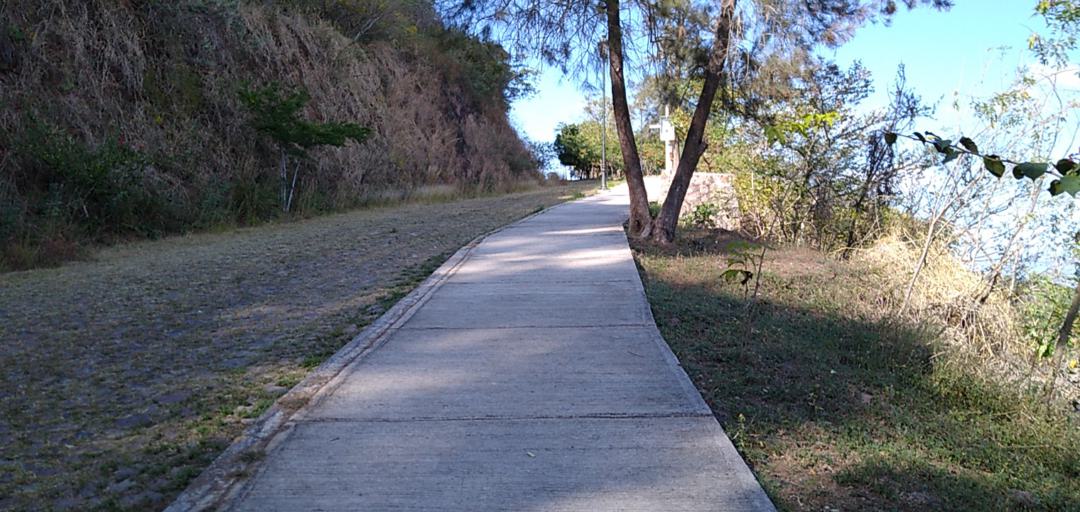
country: MX
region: Nayarit
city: Tepic
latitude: 21.5329
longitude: -104.8828
